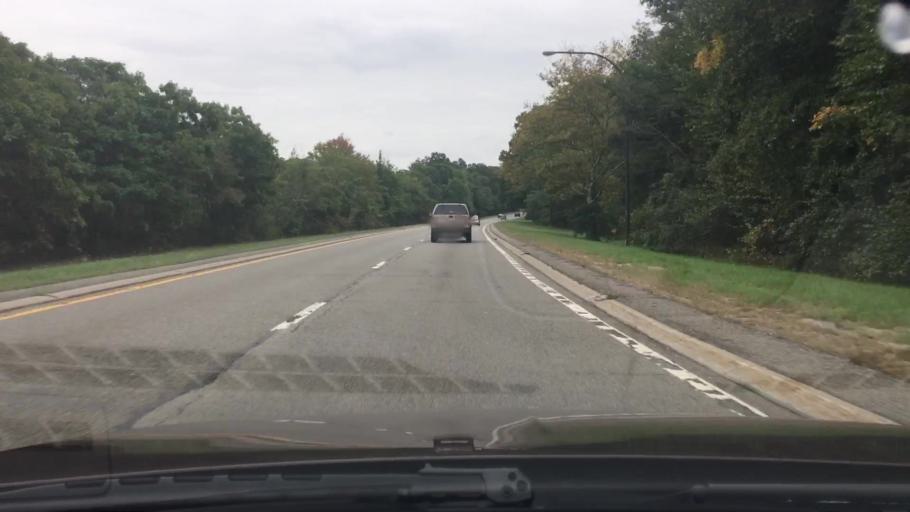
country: US
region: New York
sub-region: Suffolk County
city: Elwood
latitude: 40.8273
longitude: -73.3327
